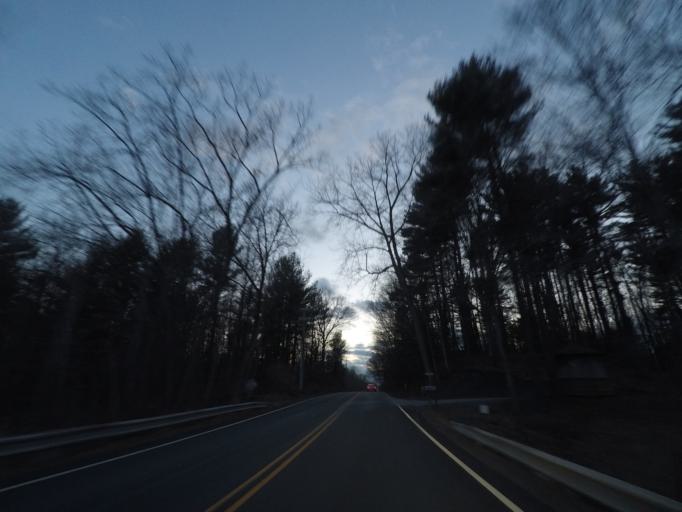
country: US
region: New York
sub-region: Schenectady County
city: Niskayuna
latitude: 42.8323
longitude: -73.8114
